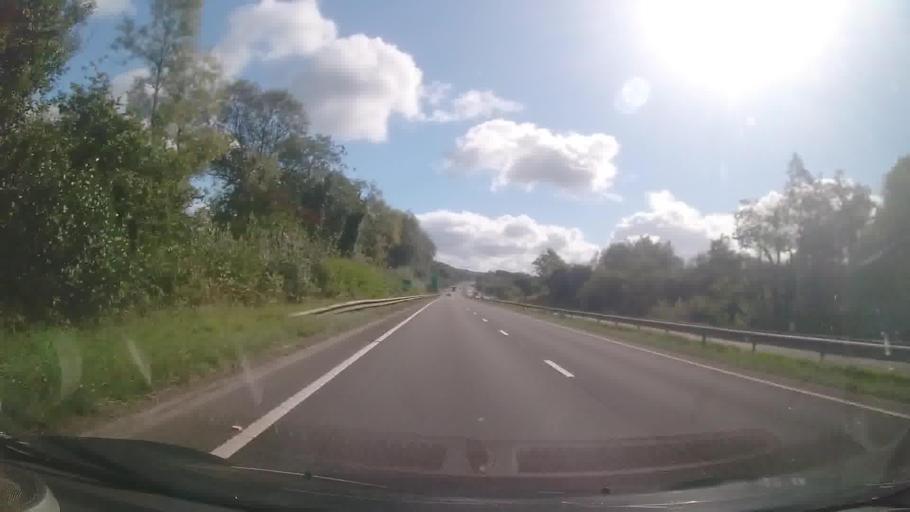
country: GB
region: Wales
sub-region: Carmarthenshire
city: Llanddarog
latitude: 51.8300
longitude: -4.1548
